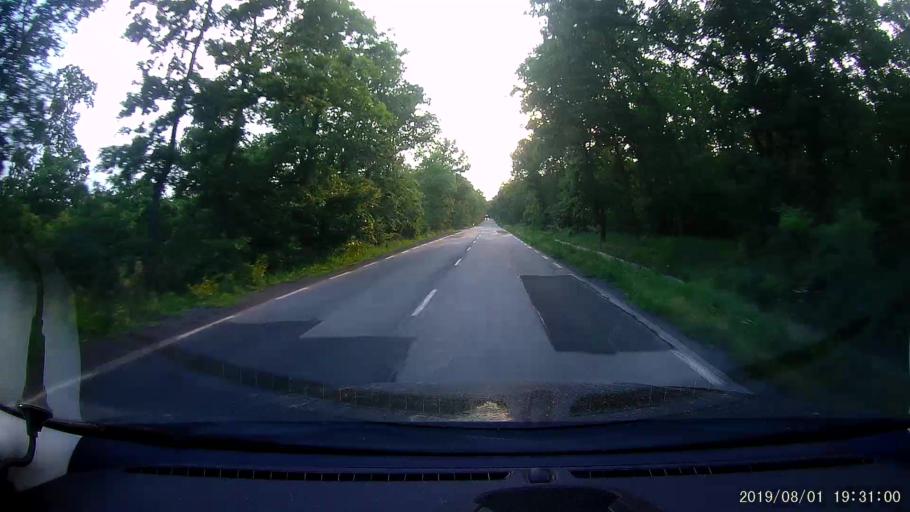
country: BG
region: Burgas
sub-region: Obshtina Sungurlare
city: Sungurlare
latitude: 42.8102
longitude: 26.8828
